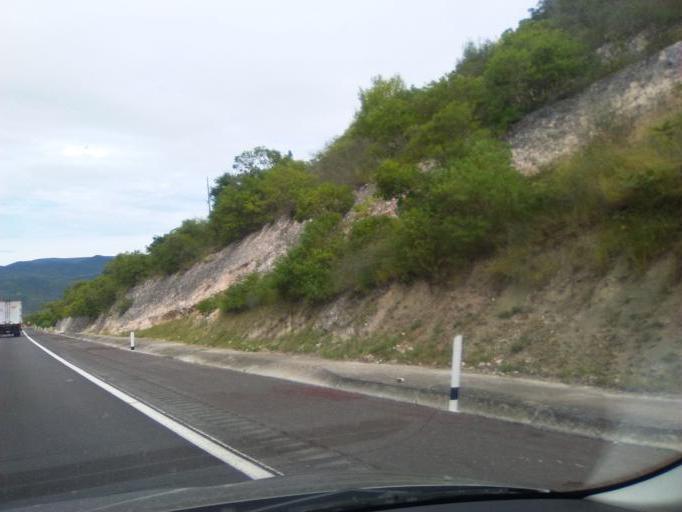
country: MX
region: Guerrero
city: Zumpango del Rio
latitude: 17.6237
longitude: -99.5155
